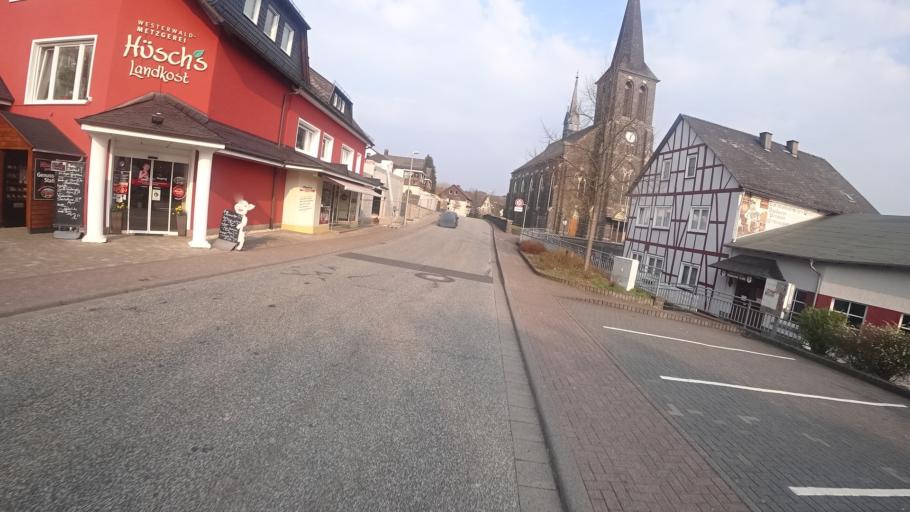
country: DE
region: Rheinland-Pfalz
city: Luckenbach
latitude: 50.7126
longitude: 7.8478
